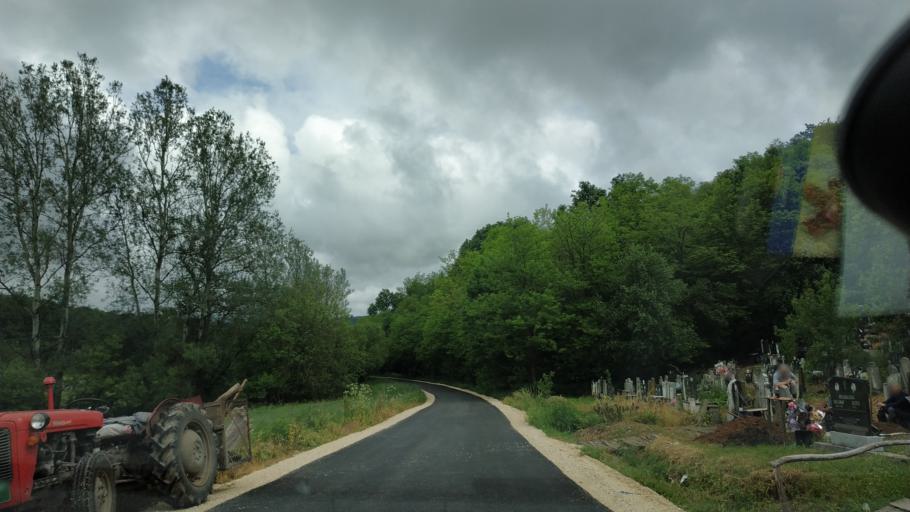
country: RS
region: Central Serbia
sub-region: Zajecarski Okrug
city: Soko Banja
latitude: 43.6633
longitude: 21.9106
